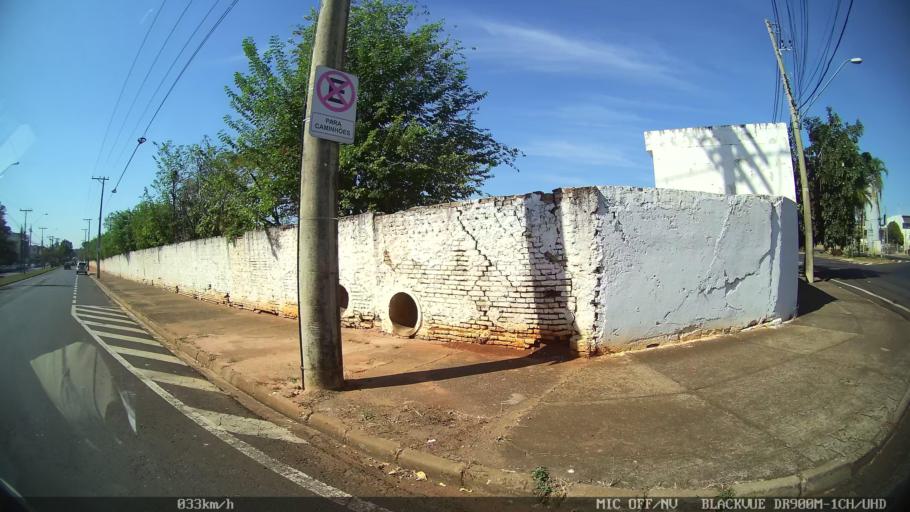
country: BR
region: Sao Paulo
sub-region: Sao Jose Do Rio Preto
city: Sao Jose do Rio Preto
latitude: -20.8106
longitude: -49.4114
